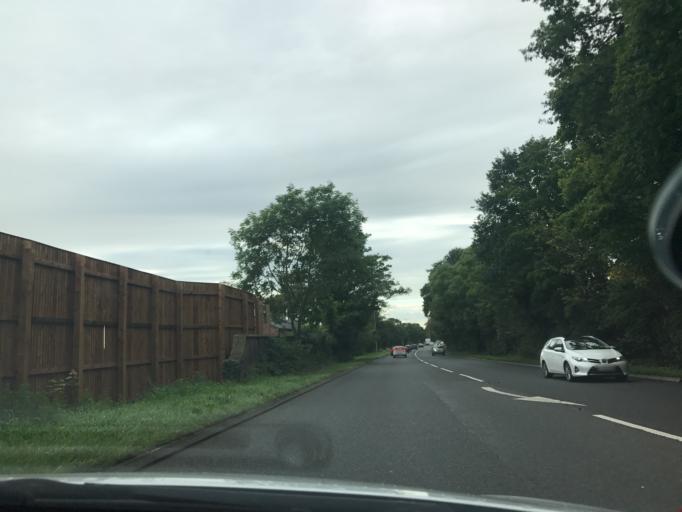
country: GB
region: England
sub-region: Cheshire West and Chester
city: Tarvin
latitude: 53.1955
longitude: -2.7829
